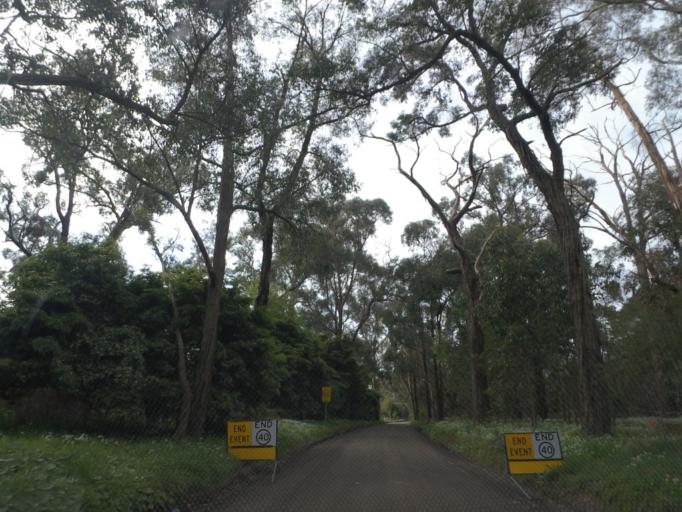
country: AU
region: Victoria
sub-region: Knox
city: The Basin
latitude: -37.8465
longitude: 145.3261
